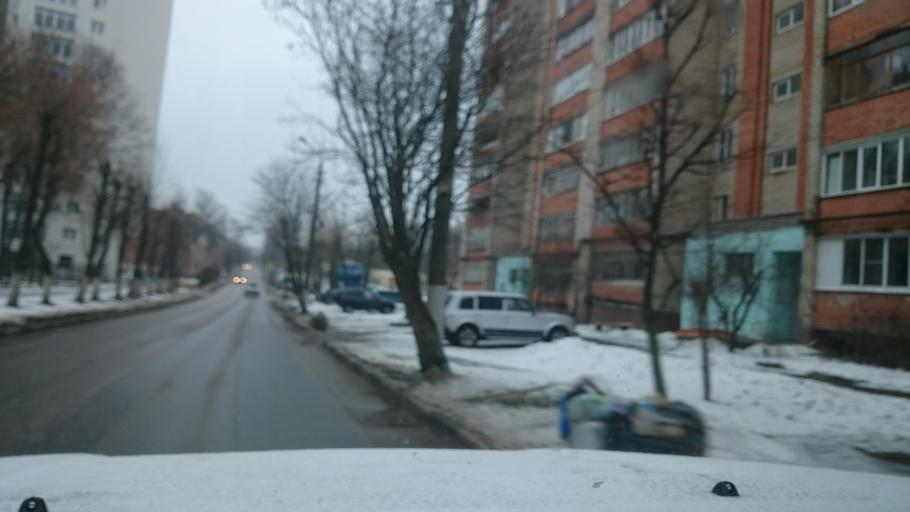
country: RU
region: Tula
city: Mendeleyevskiy
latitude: 54.1743
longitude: 37.5784
